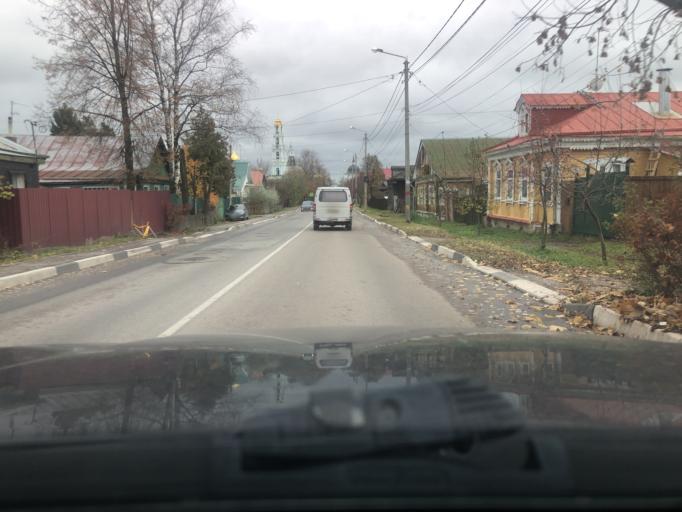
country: RU
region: Moskovskaya
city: Sergiyev Posad
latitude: 56.3154
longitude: 38.1247
